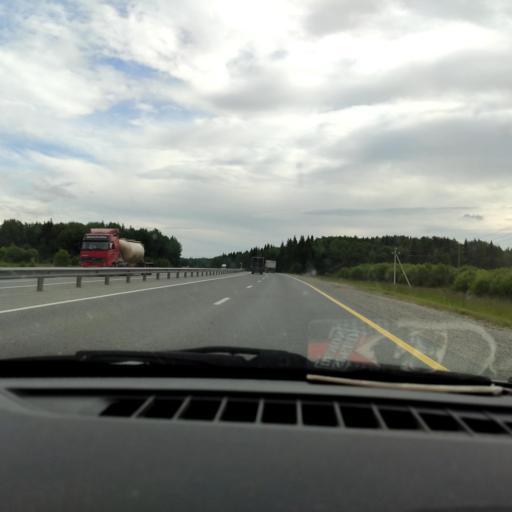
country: RU
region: Perm
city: Polazna
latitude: 58.2633
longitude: 56.4105
